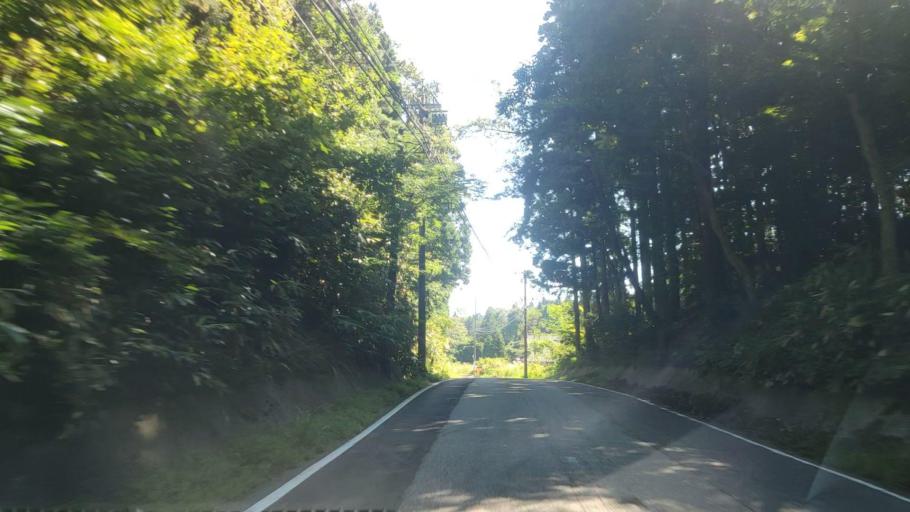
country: JP
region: Ishikawa
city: Nanao
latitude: 37.4580
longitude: 137.3025
